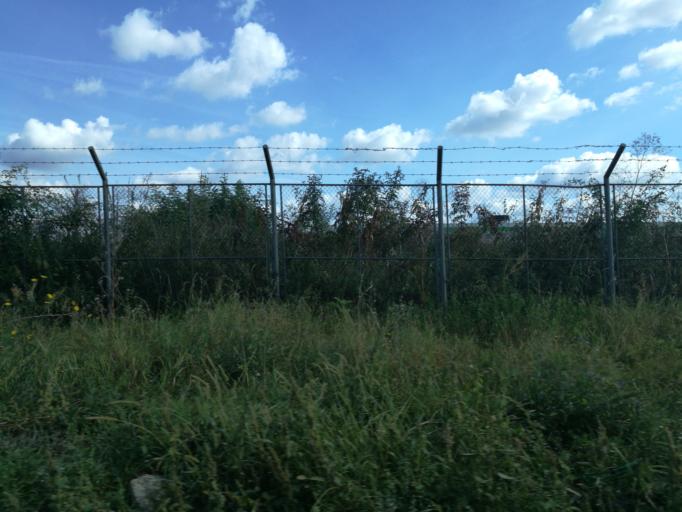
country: RO
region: Bihor
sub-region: Comuna Biharea
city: Oradea
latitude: 47.0448
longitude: 21.9070
